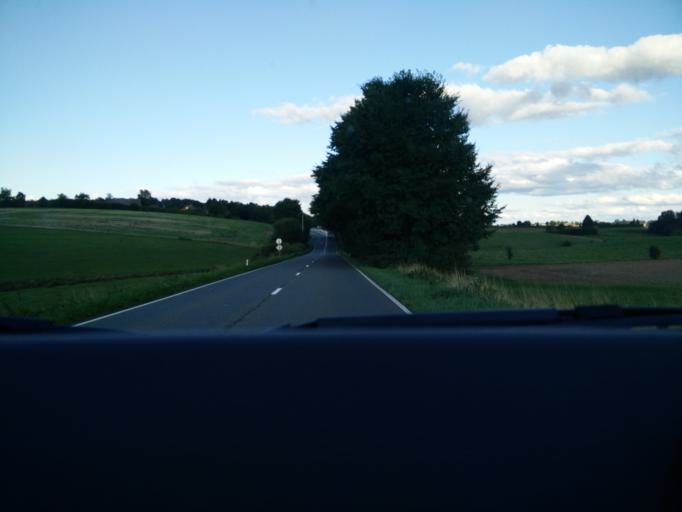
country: BE
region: Wallonia
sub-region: Province de Namur
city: Onhaye
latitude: 50.2419
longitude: 4.8194
